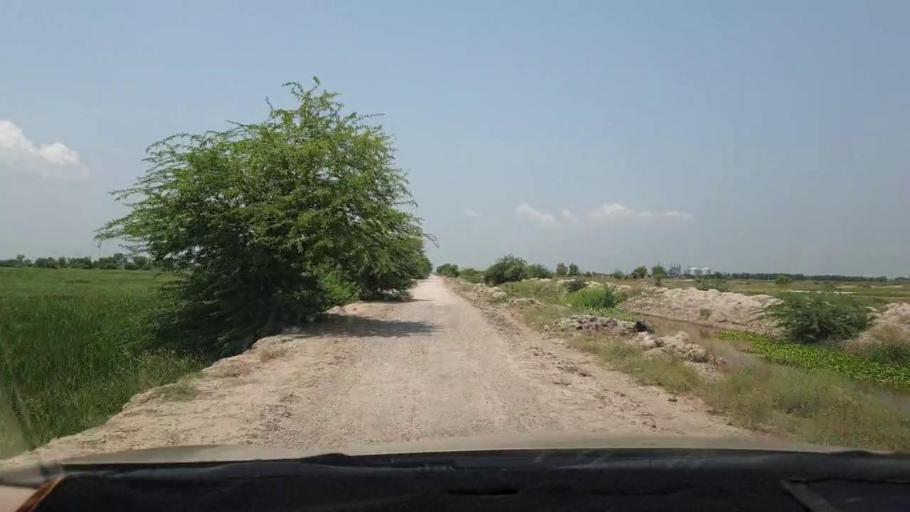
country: PK
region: Sindh
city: Naudero
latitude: 27.6619
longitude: 68.2700
